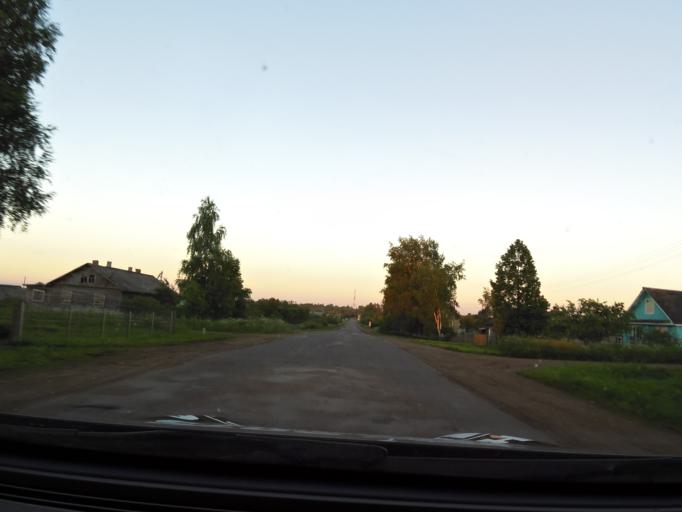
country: RU
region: Leningrad
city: Voznesen'ye
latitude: 60.8579
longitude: 35.5416
